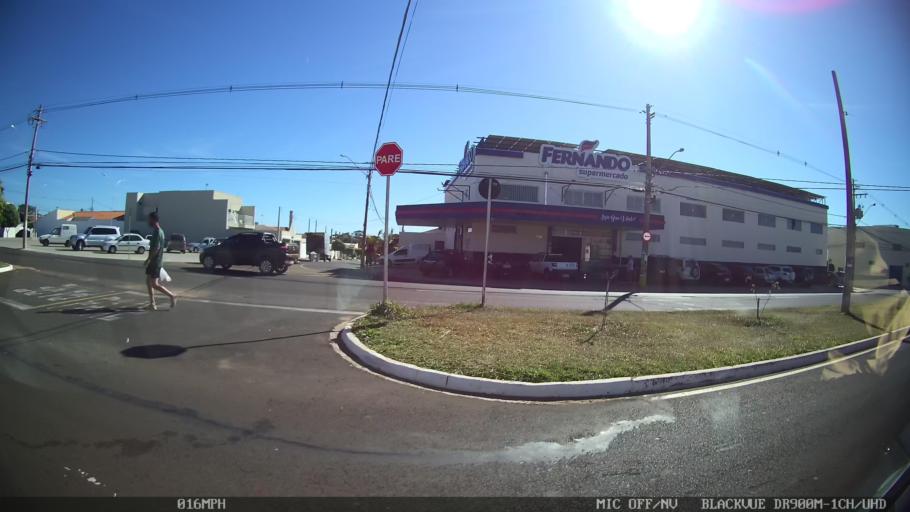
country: BR
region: Sao Paulo
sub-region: Franca
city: Franca
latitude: -20.5643
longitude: -47.3543
